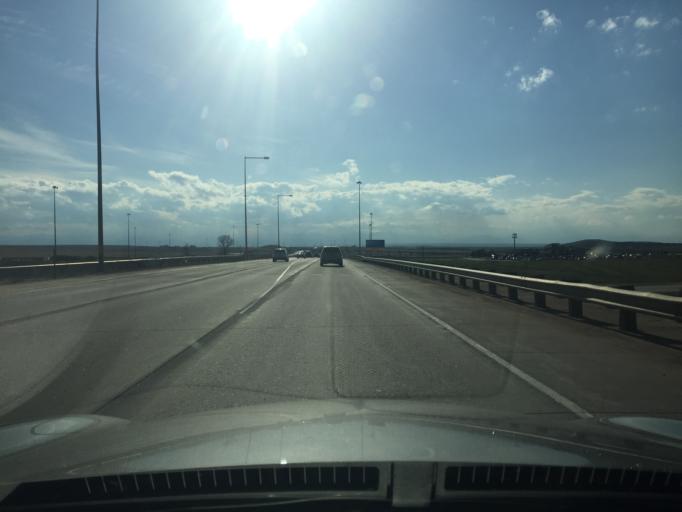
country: US
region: Colorado
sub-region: Adams County
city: Aurora
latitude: 39.8345
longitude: -104.7143
